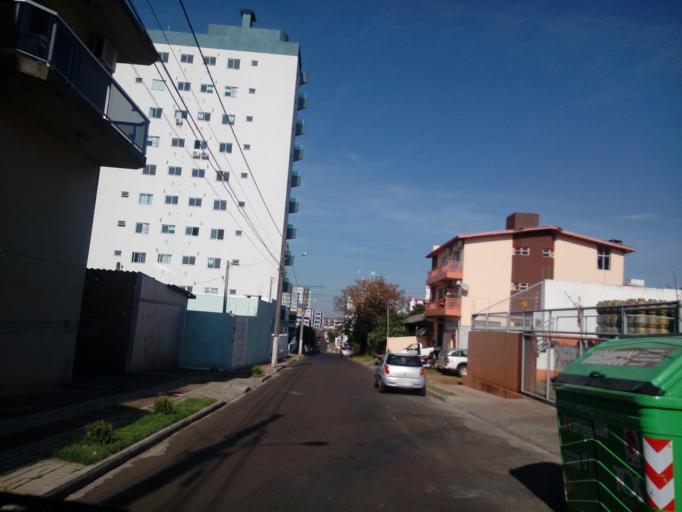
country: BR
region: Santa Catarina
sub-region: Chapeco
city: Chapeco
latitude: -27.0933
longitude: -52.6271
